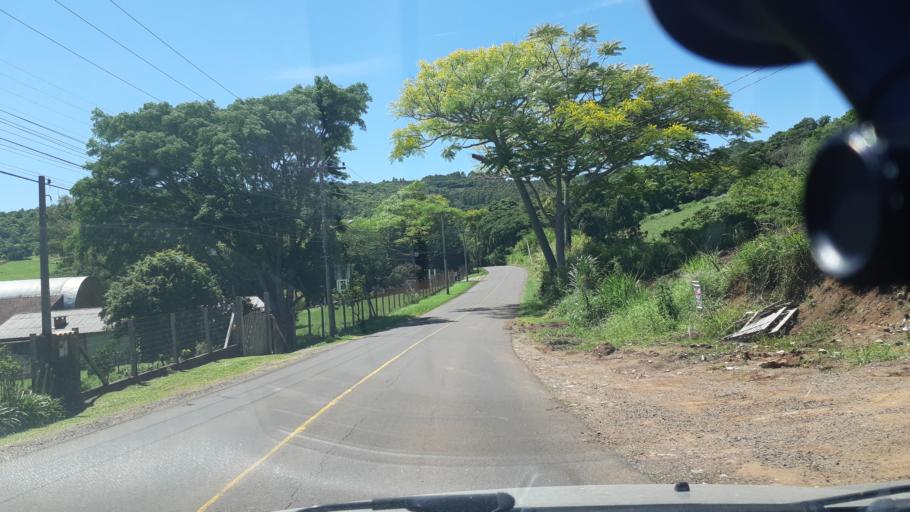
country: BR
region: Rio Grande do Sul
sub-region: Novo Hamburgo
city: Novo Hamburgo
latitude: -29.6262
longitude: -51.0979
